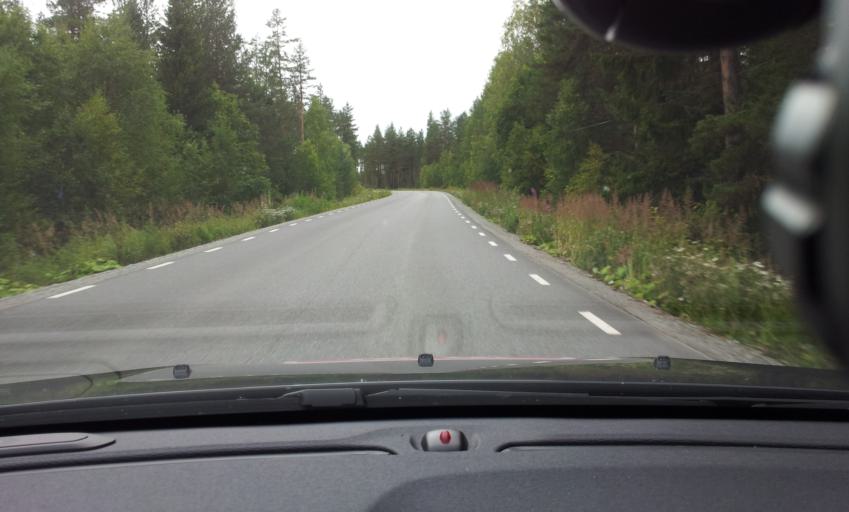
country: SE
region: Jaemtland
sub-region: Braecke Kommun
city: Braecke
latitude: 63.1620
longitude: 15.5653
